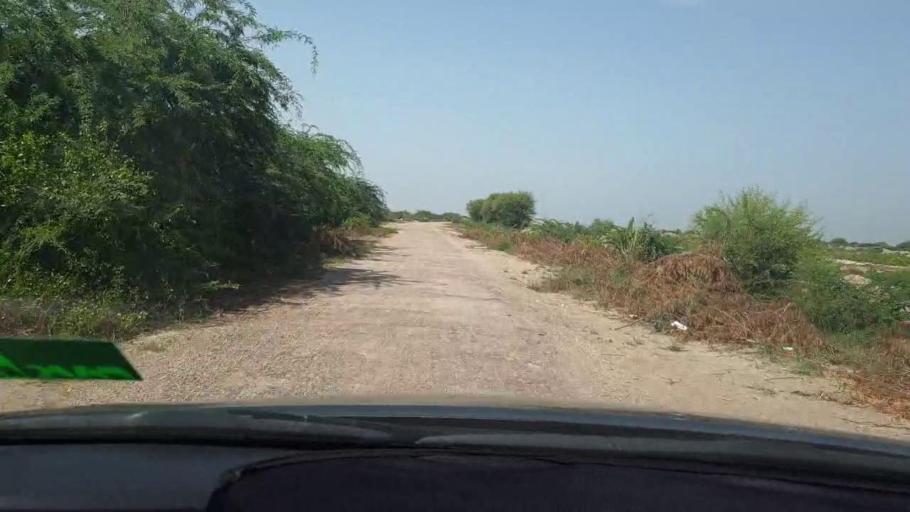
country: PK
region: Sindh
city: Digri
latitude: 24.9392
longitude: 69.1460
